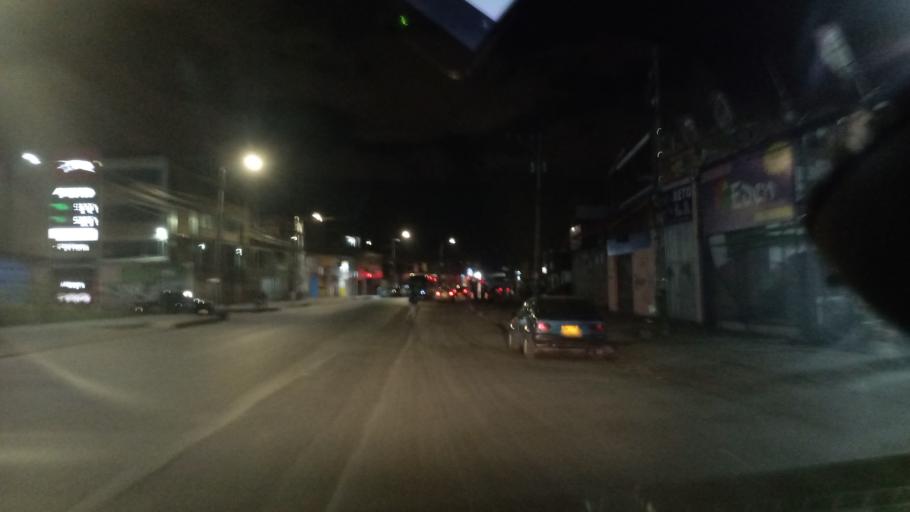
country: CO
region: Cundinamarca
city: Funza
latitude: 4.6792
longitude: -74.1512
